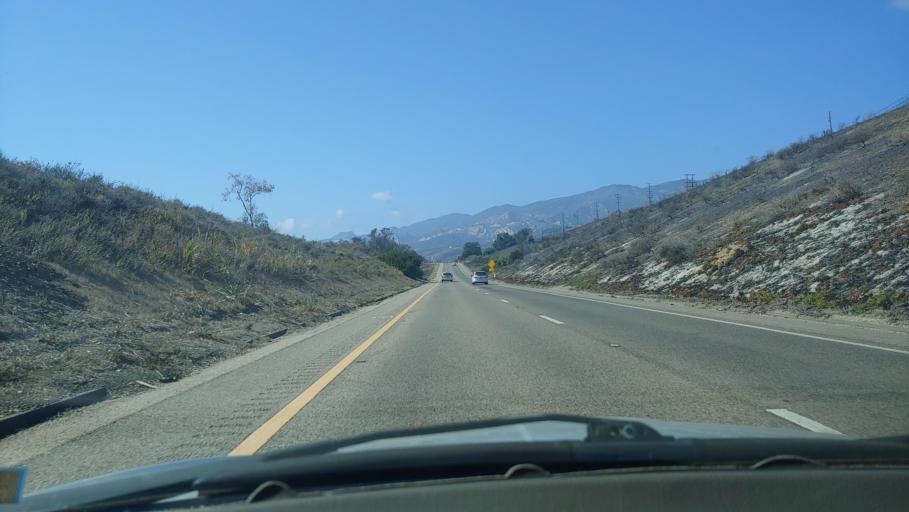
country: US
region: California
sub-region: Santa Barbara County
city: Solvang
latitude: 34.4637
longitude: -120.0975
